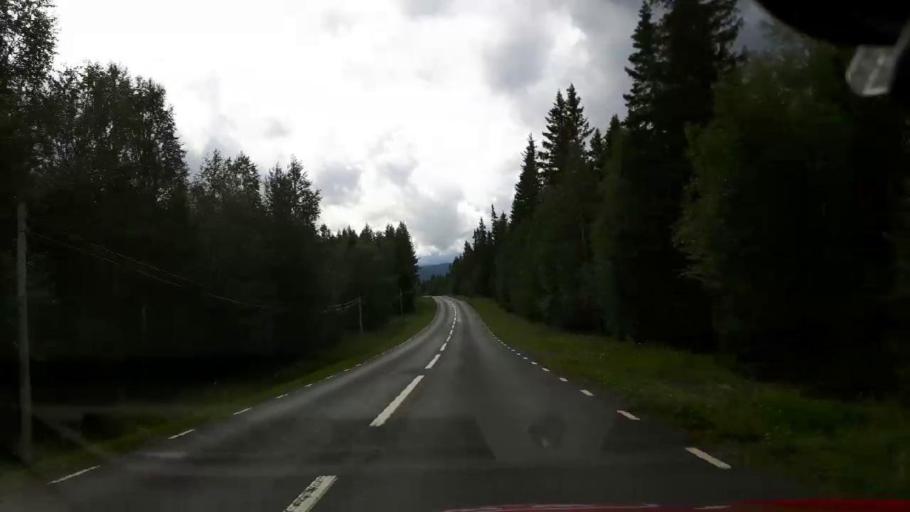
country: NO
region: Nord-Trondelag
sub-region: Lierne
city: Sandvika
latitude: 64.5170
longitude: 14.1603
